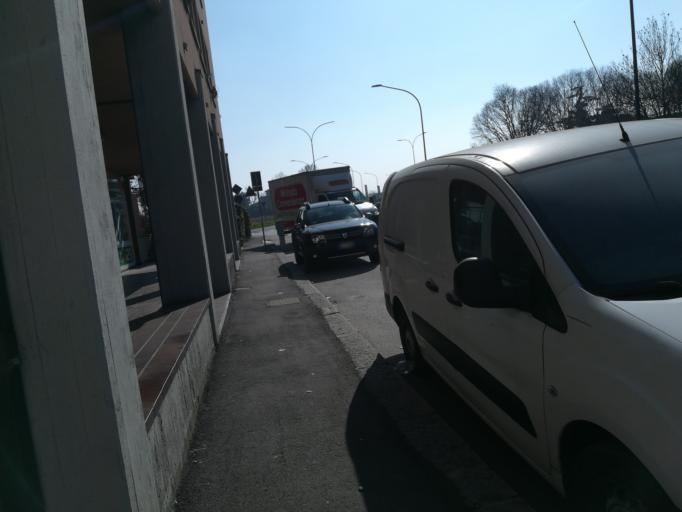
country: IT
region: Emilia-Romagna
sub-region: Provincia di Bologna
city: Progresso
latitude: 44.5401
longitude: 11.3580
